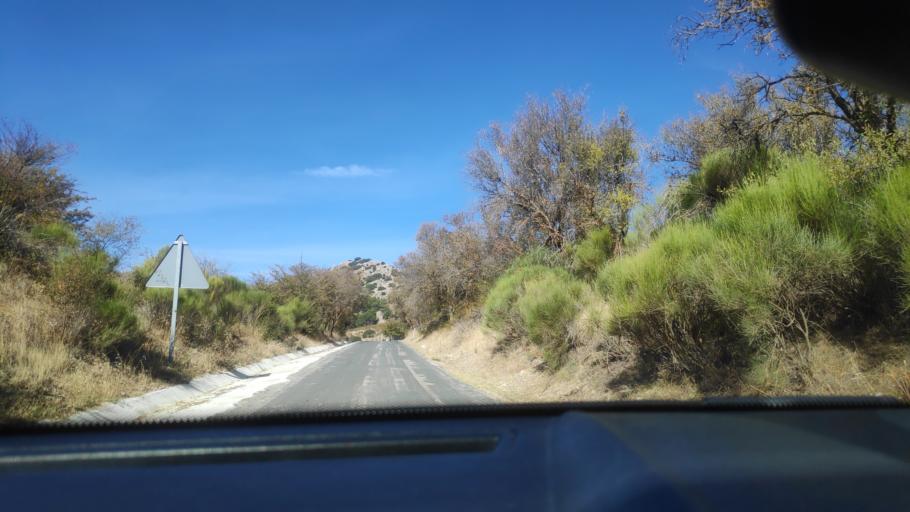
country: ES
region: Andalusia
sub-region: Provincia de Jaen
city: Torres
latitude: 37.7859
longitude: -3.4821
